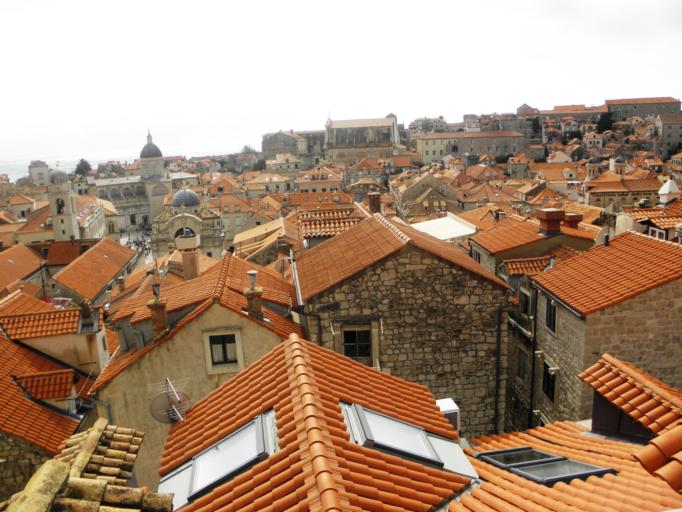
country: HR
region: Dubrovacko-Neretvanska
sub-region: Grad Dubrovnik
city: Dubrovnik
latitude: 42.6426
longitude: 18.1091
